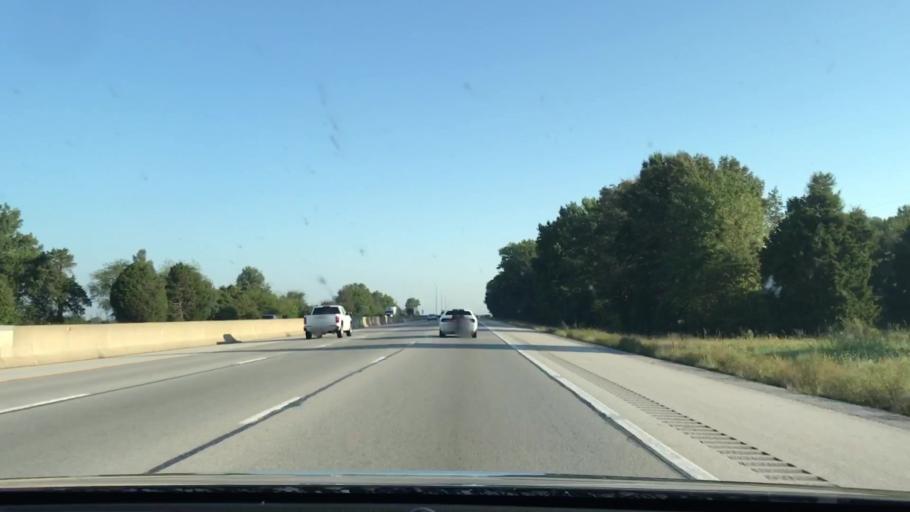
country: US
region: Kentucky
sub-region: Warren County
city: Plano
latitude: 36.8931
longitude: -86.4400
